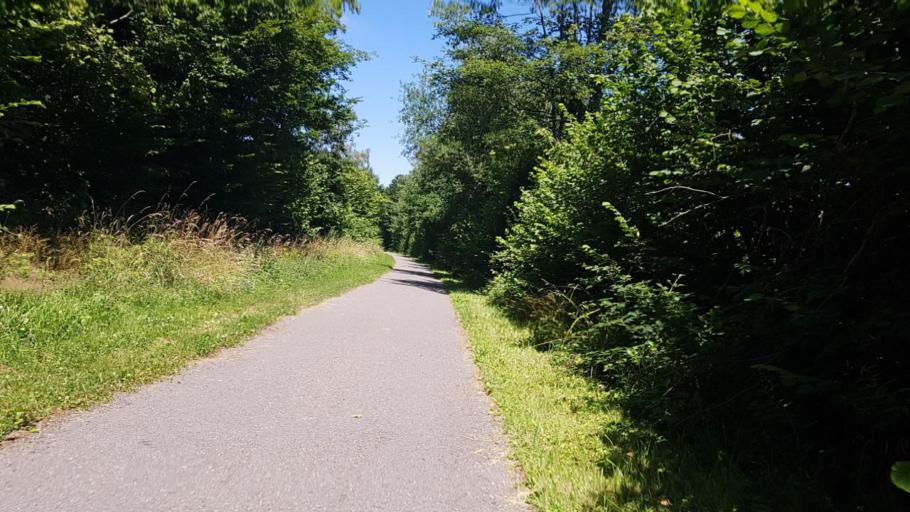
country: BE
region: Wallonia
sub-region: Province du Hainaut
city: Beaumont
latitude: 50.2082
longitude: 4.2351
